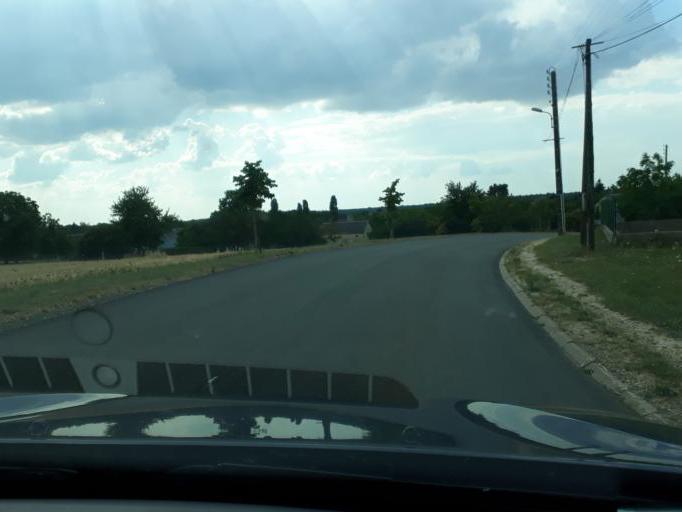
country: FR
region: Centre
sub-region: Departement du Cher
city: Baugy
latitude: 47.0939
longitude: 2.6797
